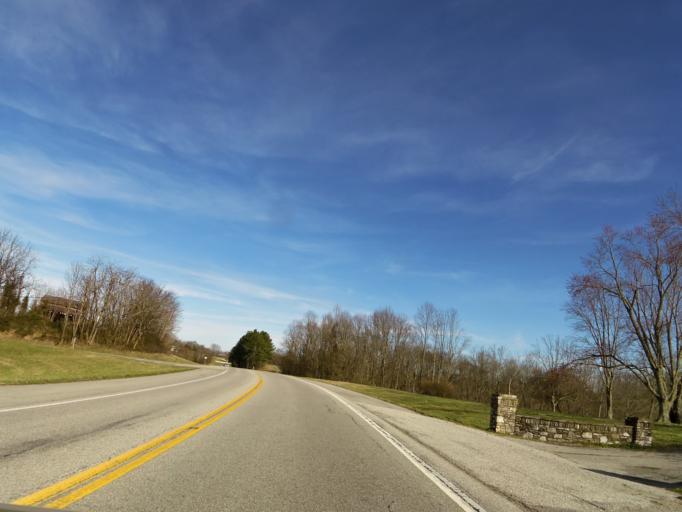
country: US
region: Tennessee
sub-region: Cannon County
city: Woodbury
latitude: 35.8036
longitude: -86.0186
